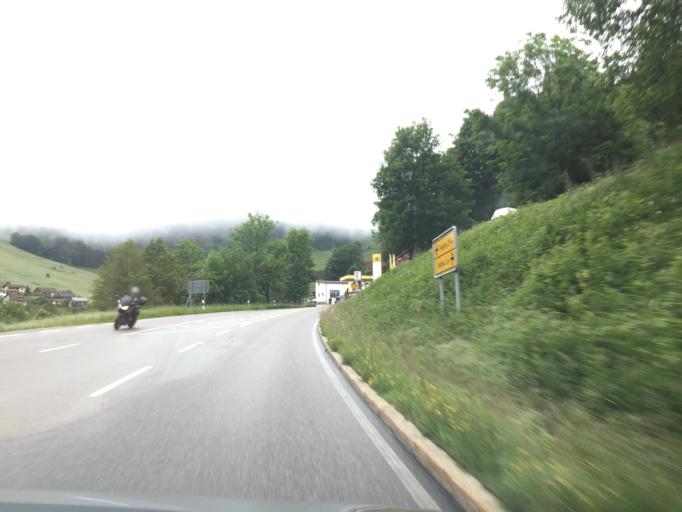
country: DE
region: Baden-Wuerttemberg
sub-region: Freiburg Region
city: Todtnau
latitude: 47.8417
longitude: 7.9320
